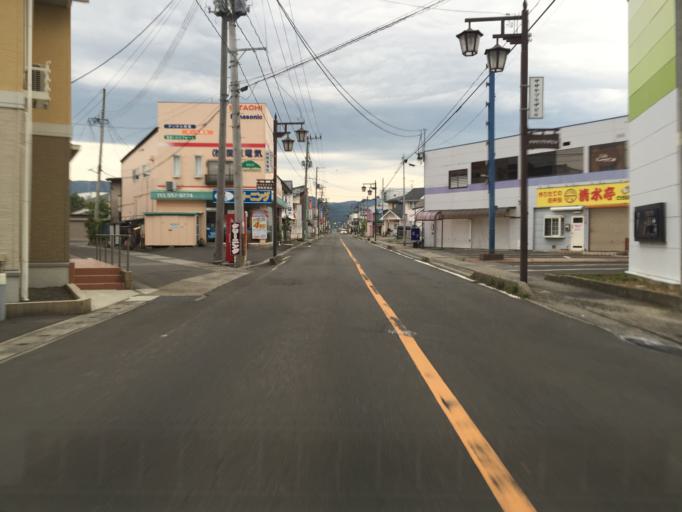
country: JP
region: Fukushima
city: Fukushima-shi
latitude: 37.7873
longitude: 140.4377
